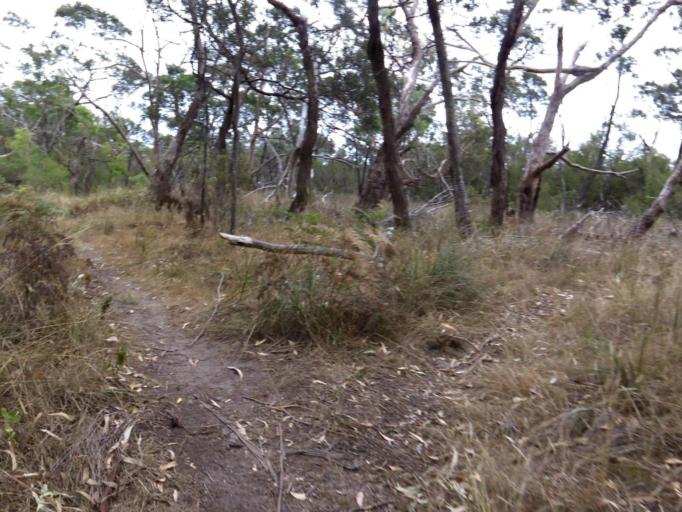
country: AU
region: Victoria
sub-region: Mornington Peninsula
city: Mount Martha
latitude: -38.2864
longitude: 145.0091
